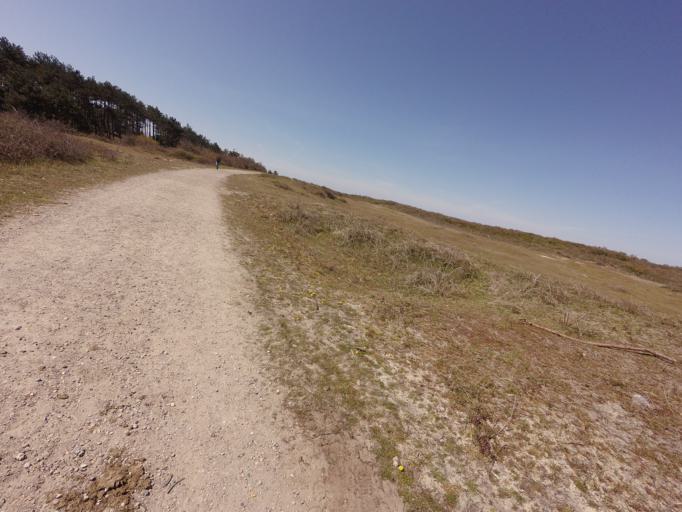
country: NL
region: Zeeland
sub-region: Gemeente Middelburg
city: Middelburg
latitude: 51.5907
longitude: 3.5697
